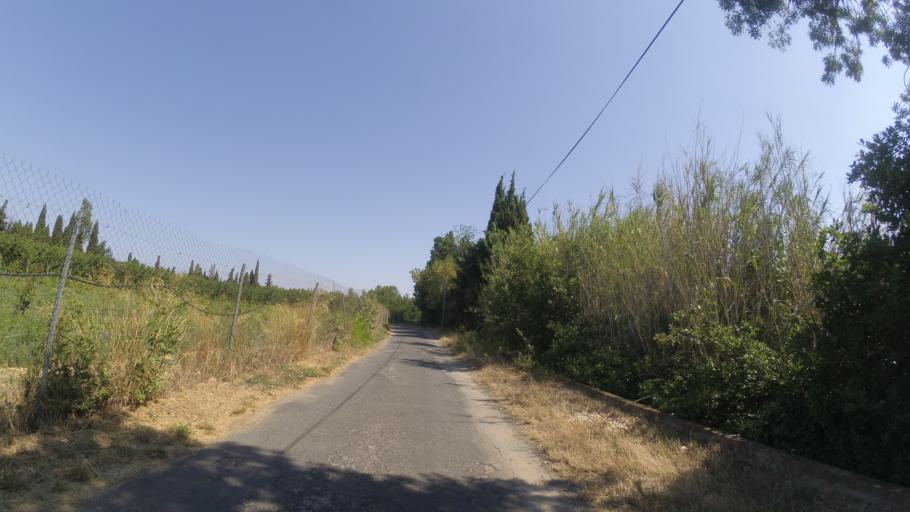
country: FR
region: Languedoc-Roussillon
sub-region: Departement des Pyrenees-Orientales
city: Corneilla-la-Riviere
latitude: 42.6652
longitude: 2.7261
